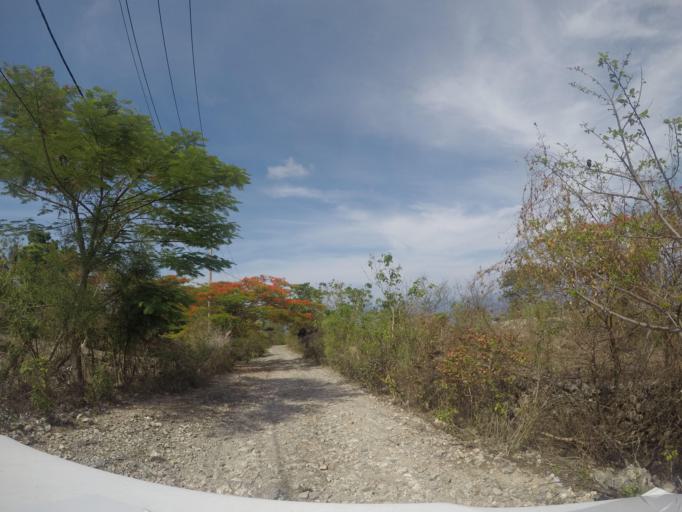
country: TL
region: Baucau
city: Baucau
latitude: -8.4688
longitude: 126.4654
